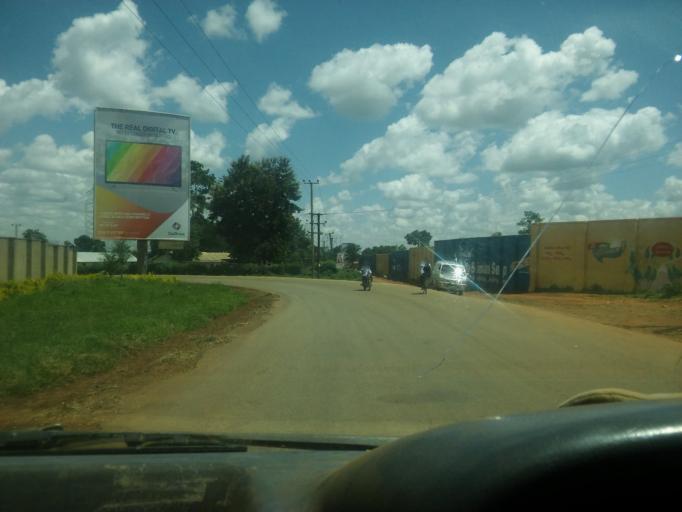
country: UG
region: Eastern Region
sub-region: Mbale District
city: Mbale
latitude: 1.0797
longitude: 34.1572
